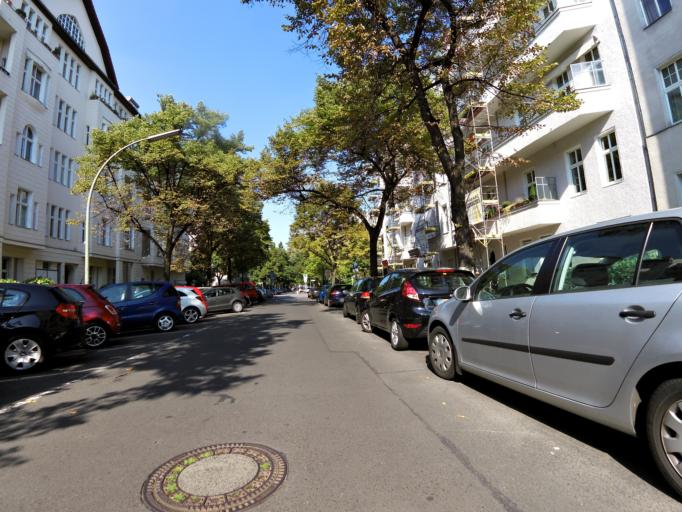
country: DE
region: Berlin
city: Berlin Schoeneberg
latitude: 52.4901
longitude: 13.3331
